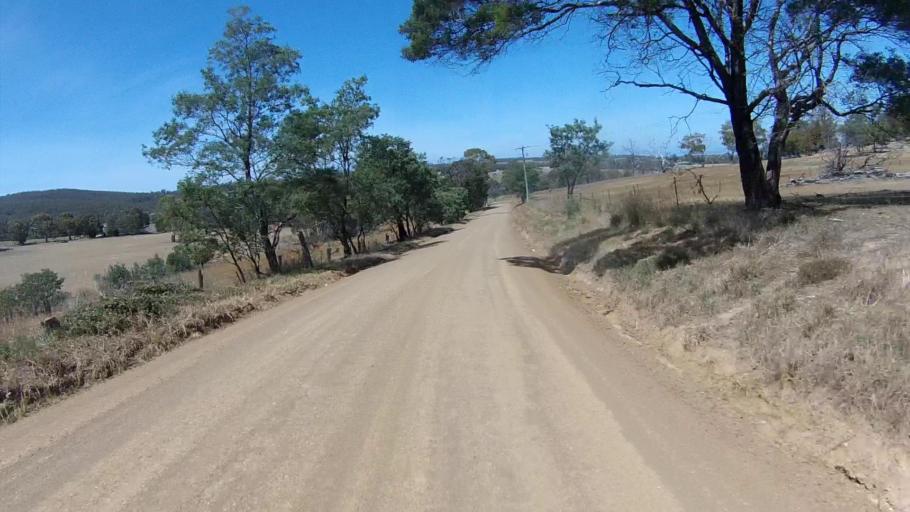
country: AU
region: Tasmania
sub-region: Sorell
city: Sorell
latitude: -42.7958
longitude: 147.6406
